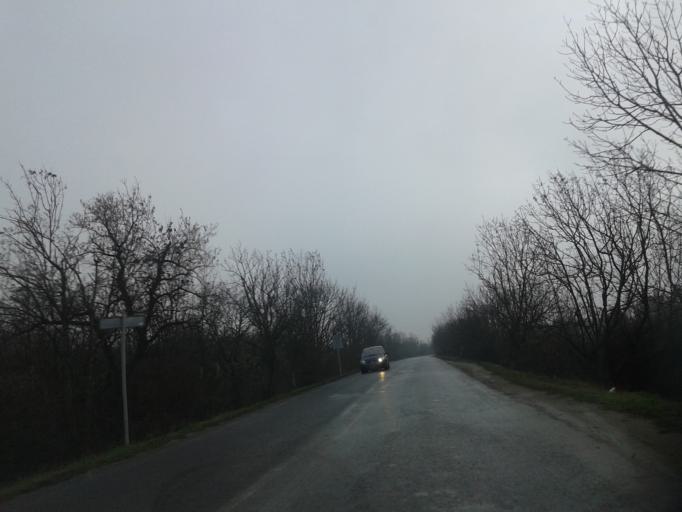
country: HU
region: Pest
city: Diosd
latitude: 47.4220
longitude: 18.9770
